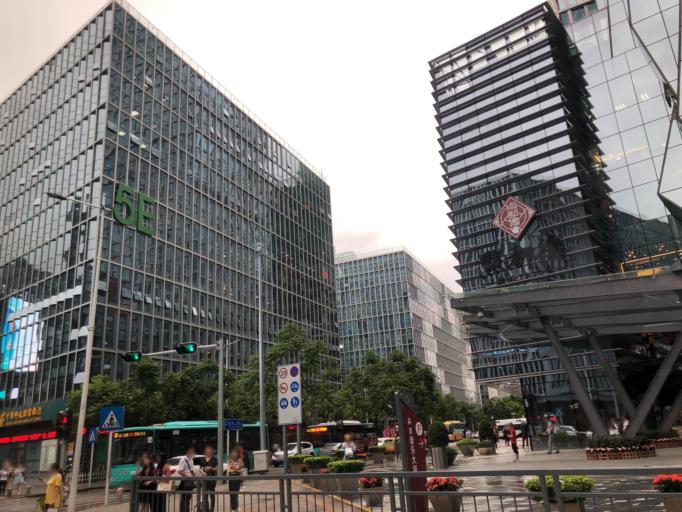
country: CN
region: Guangdong
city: Haikuotiankong
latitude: 22.5255
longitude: 113.9337
